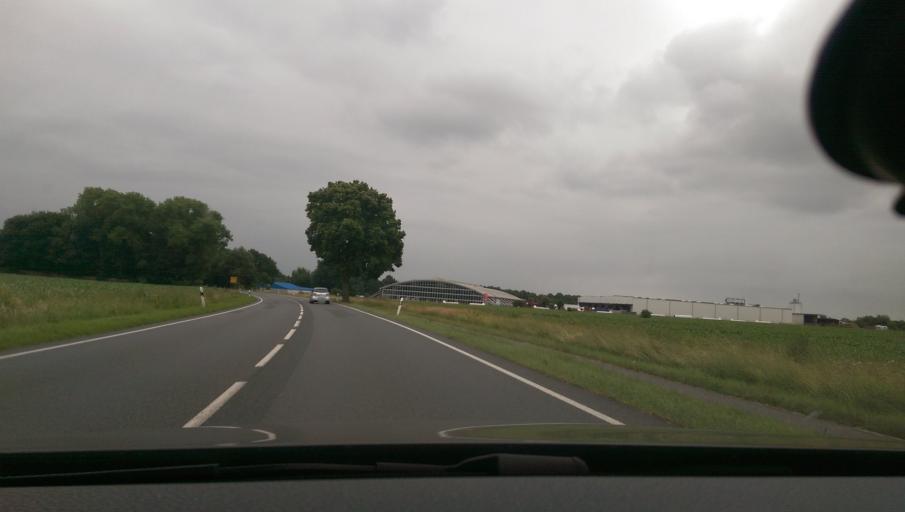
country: DE
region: Lower Saxony
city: Botersen
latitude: 53.1296
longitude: 9.3643
